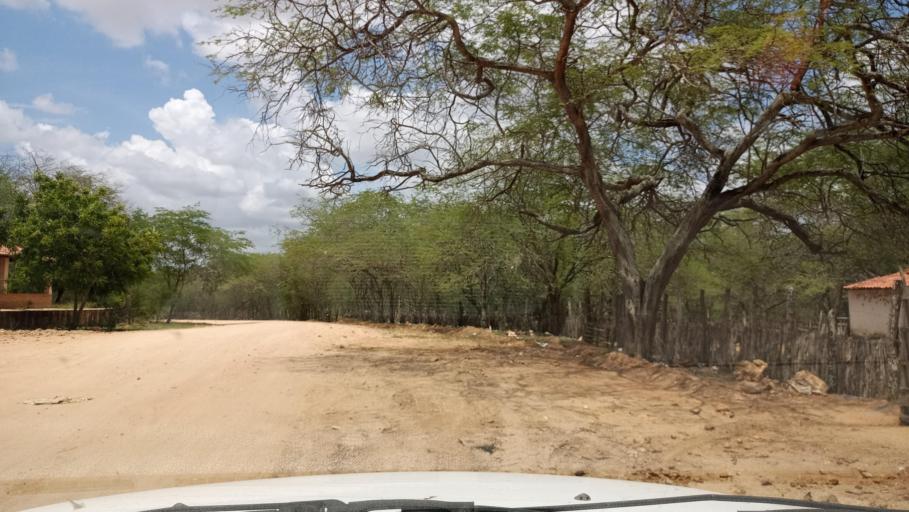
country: BR
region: Rio Grande do Norte
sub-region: Tangara
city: Tangara
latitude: -6.1056
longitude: -35.7157
